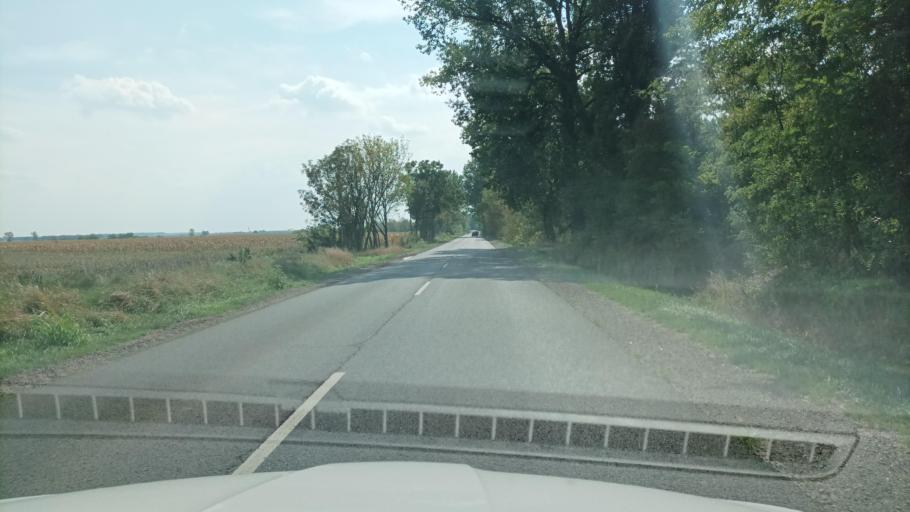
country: HU
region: Pest
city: Tura
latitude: 47.5822
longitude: 19.6023
